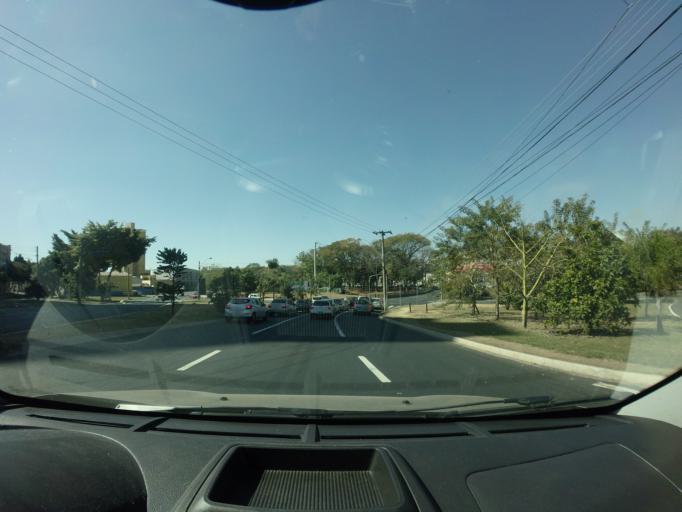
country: BR
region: Sao Paulo
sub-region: Piracicaba
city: Piracicaba
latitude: -22.7259
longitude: -47.6278
